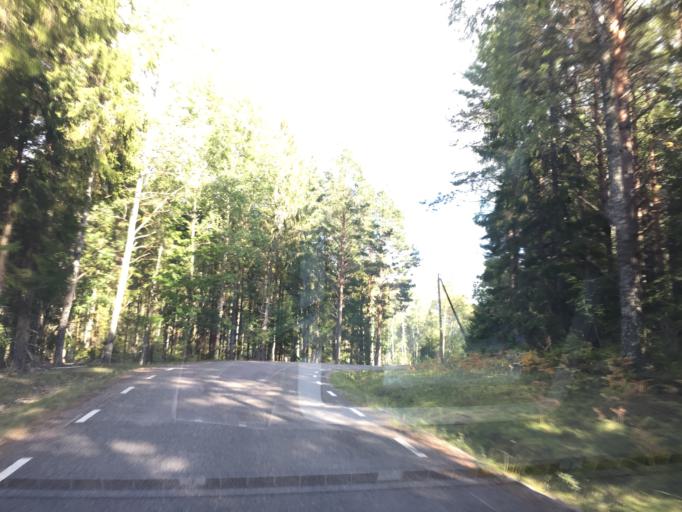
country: SE
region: Soedermanland
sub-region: Vingakers Kommun
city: Vingaker
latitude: 59.0095
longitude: 15.7098
